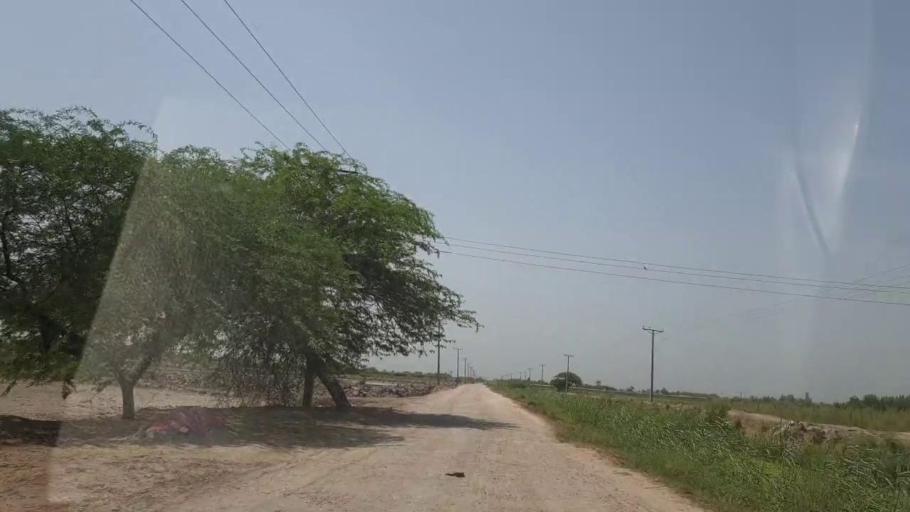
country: PK
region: Sindh
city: Ranipur
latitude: 27.3042
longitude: 68.5452
